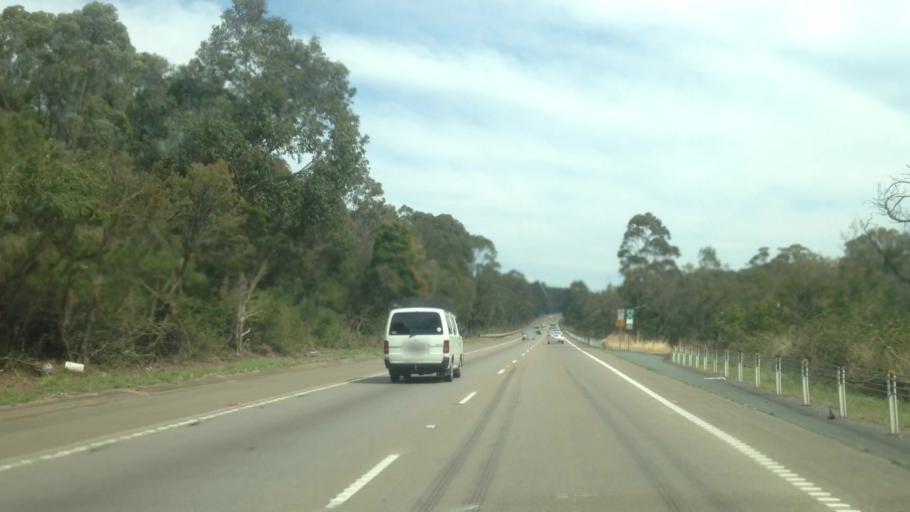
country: AU
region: New South Wales
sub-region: Lake Macquarie Shire
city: Fennell Bay
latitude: -32.9688
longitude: 151.5354
